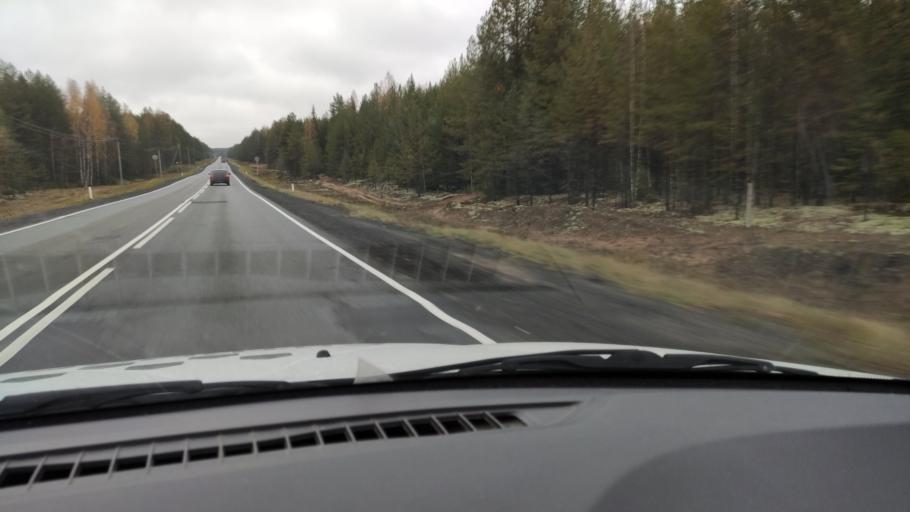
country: RU
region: Kirov
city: Belaya Kholunitsa
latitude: 58.9065
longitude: 51.0188
